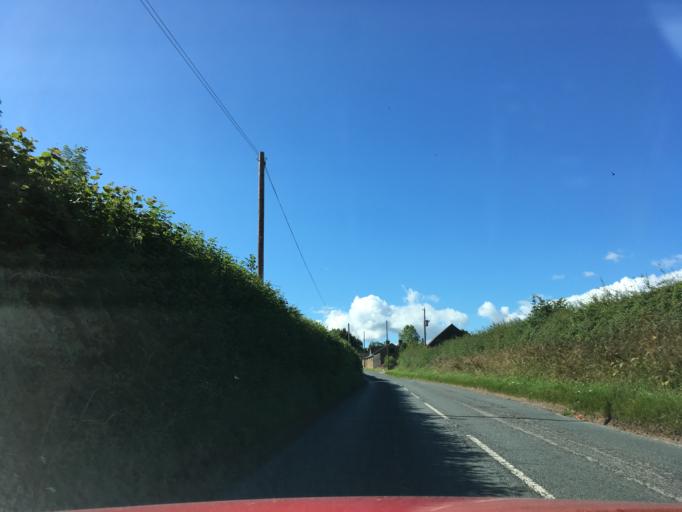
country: GB
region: England
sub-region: Herefordshire
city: Yatton
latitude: 51.9678
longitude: -2.5516
